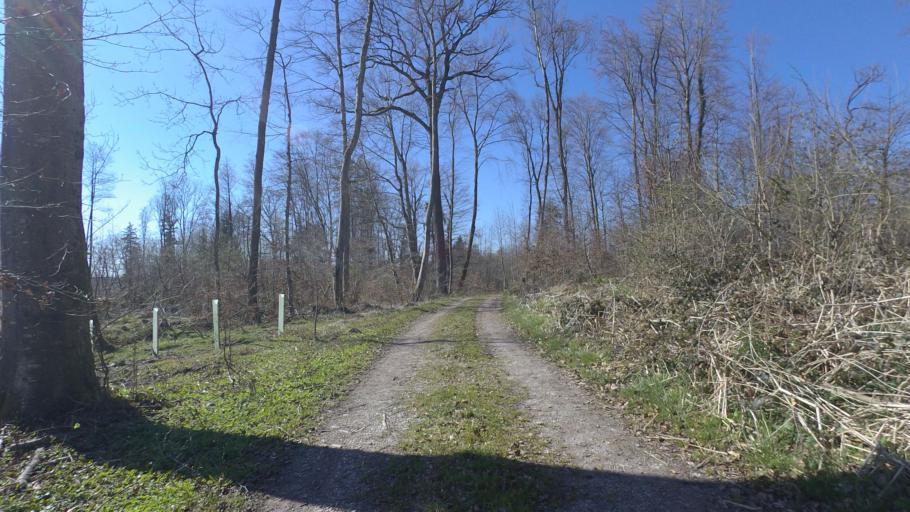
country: DE
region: Bavaria
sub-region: Upper Bavaria
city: Seeon-Seebruck
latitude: 47.9592
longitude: 12.4911
